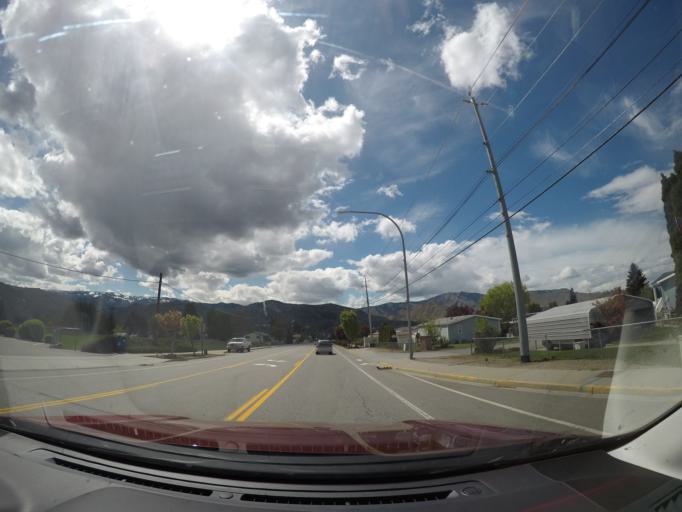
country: US
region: Washington
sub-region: Douglas County
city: East Wenatchee Bench
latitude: 47.4183
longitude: -120.2836
